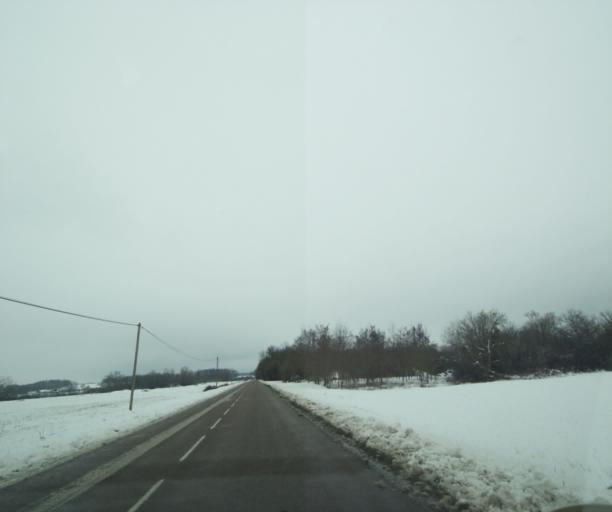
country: FR
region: Champagne-Ardenne
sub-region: Departement de la Haute-Marne
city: Montier-en-Der
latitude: 48.4500
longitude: 4.7805
